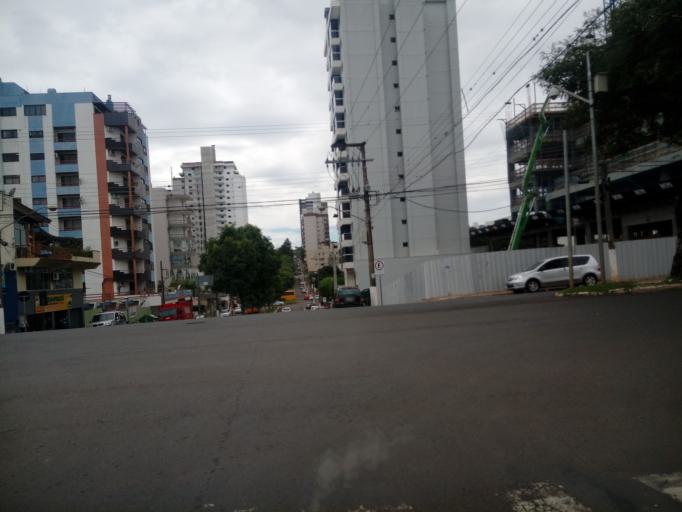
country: BR
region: Santa Catarina
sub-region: Chapeco
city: Chapeco
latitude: -27.1062
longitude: -52.6120
